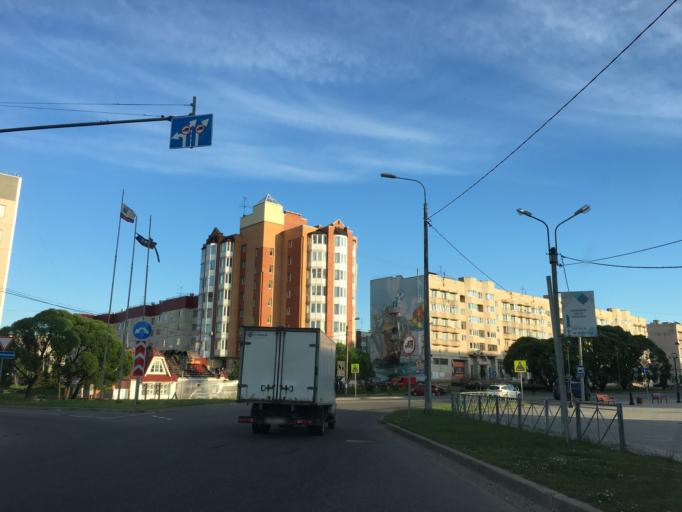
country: RU
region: Leningrad
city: Gatchina
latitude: 59.5799
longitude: 30.1376
